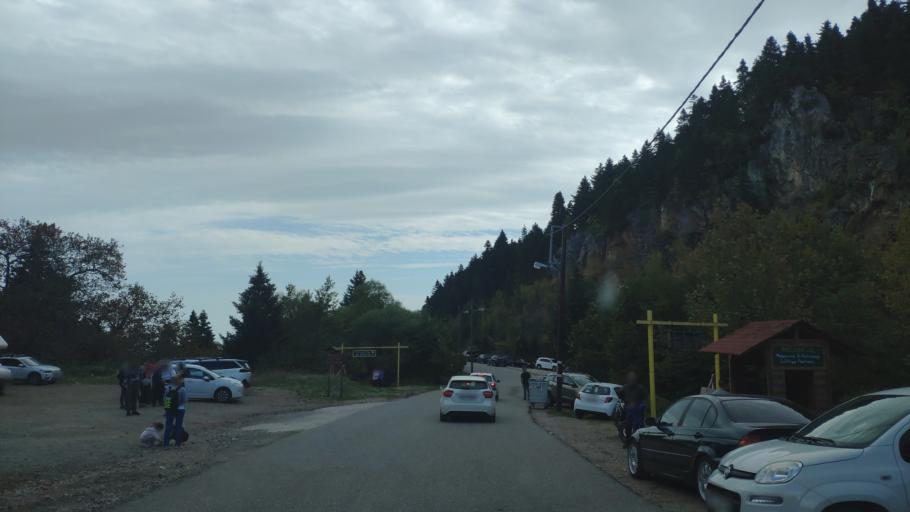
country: GR
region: Central Greece
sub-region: Nomos Fthiotidos
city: Stavros
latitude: 38.7383
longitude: 22.3408
